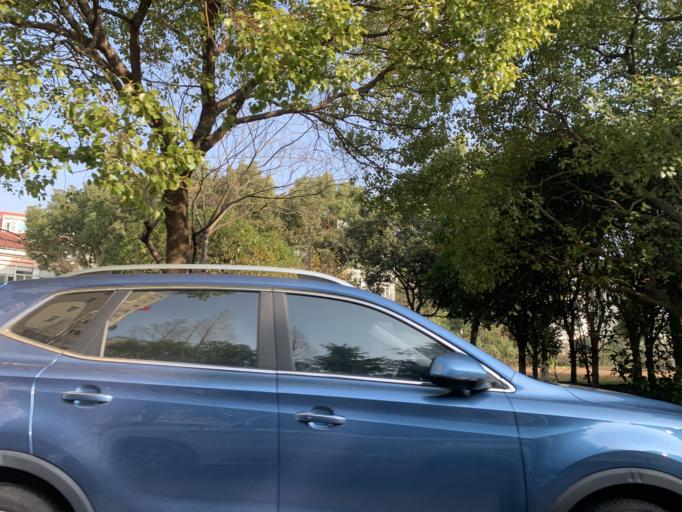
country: CN
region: Shanghai Shi
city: Huamu
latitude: 31.1885
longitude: 121.5339
